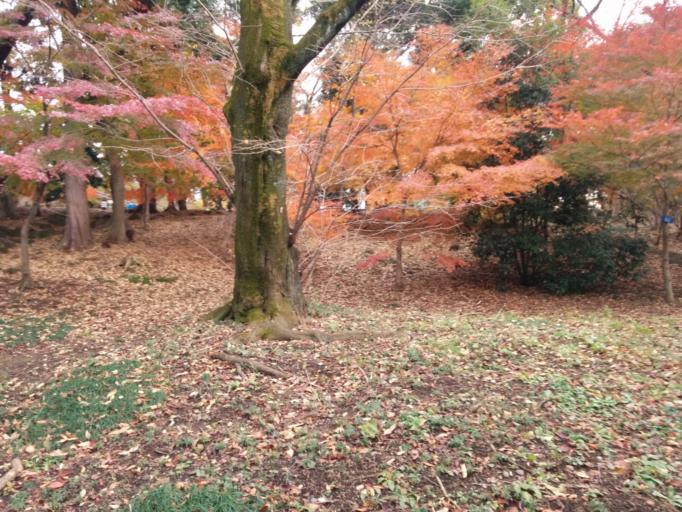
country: JP
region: Tokyo
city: Tokyo
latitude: 35.7038
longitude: 139.7128
